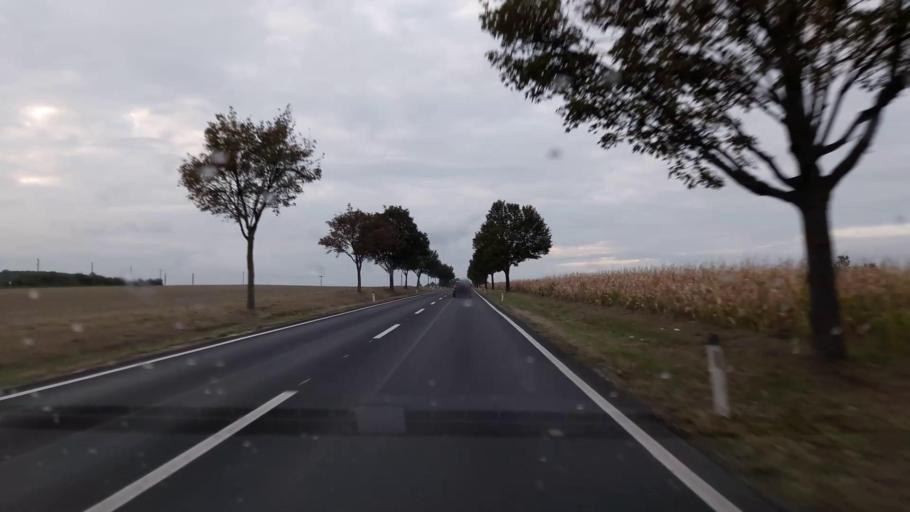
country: AT
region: Lower Austria
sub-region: Politischer Bezirk Wien-Umgebung
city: Schwadorf
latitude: 48.0786
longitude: 16.5719
